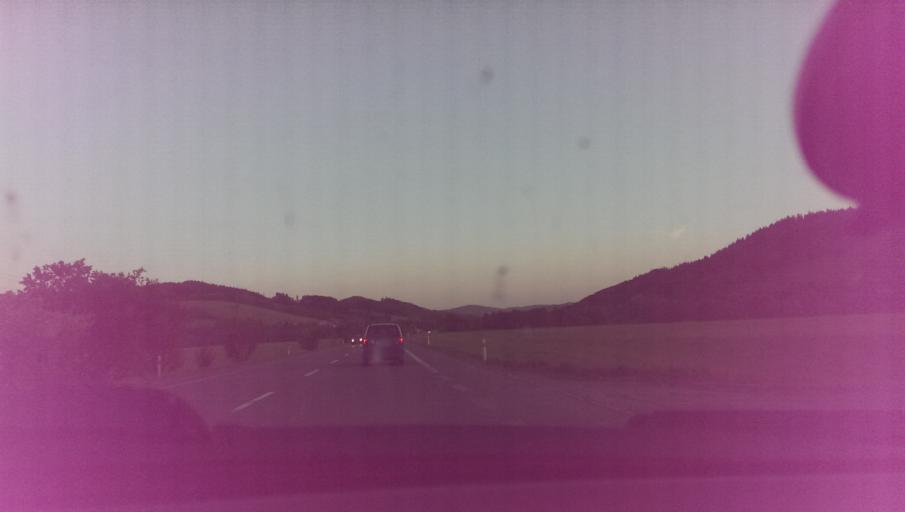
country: CZ
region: Zlin
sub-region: Okres Vsetin
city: Vsetin
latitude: 49.3182
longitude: 18.0046
